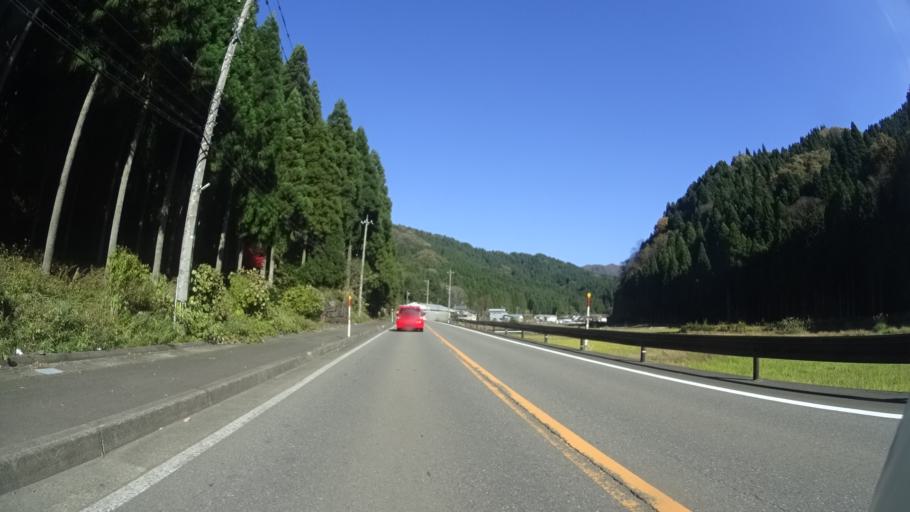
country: JP
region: Fukui
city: Ono
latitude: 36.0070
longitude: 136.3859
